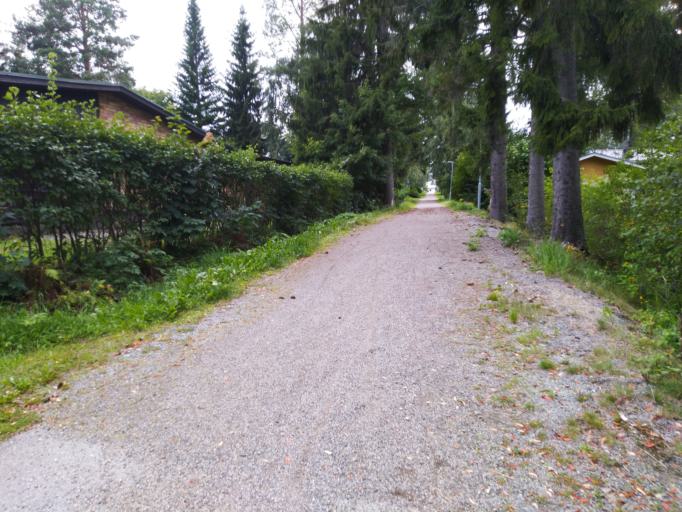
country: FI
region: North Karelia
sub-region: Joensuu
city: Joensuu
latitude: 62.5866
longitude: 29.7989
